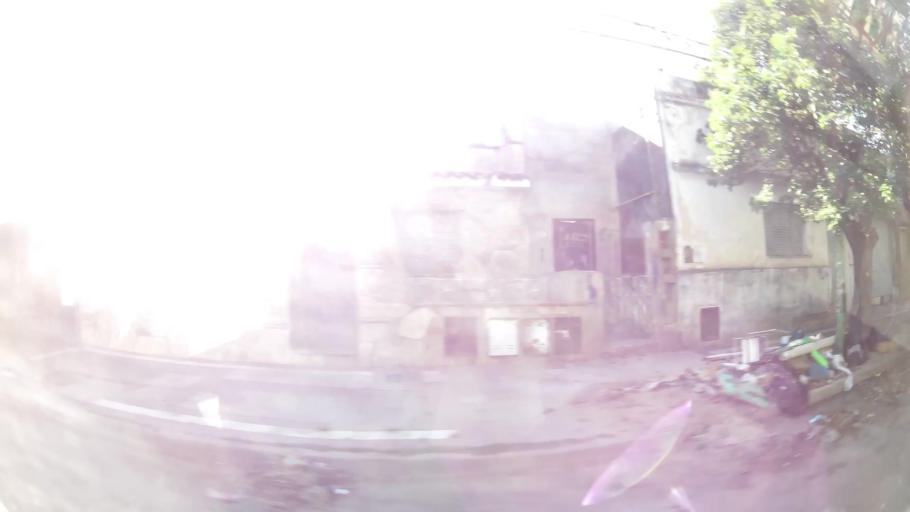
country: AR
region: Cordoba
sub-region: Departamento de Capital
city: Cordoba
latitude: -31.3891
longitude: -64.1668
